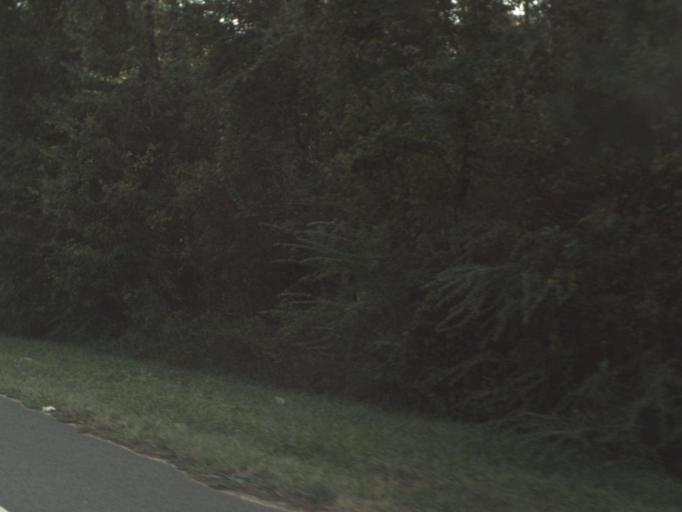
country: US
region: Florida
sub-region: Jackson County
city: Marianna
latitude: 30.6855
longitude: -85.1766
